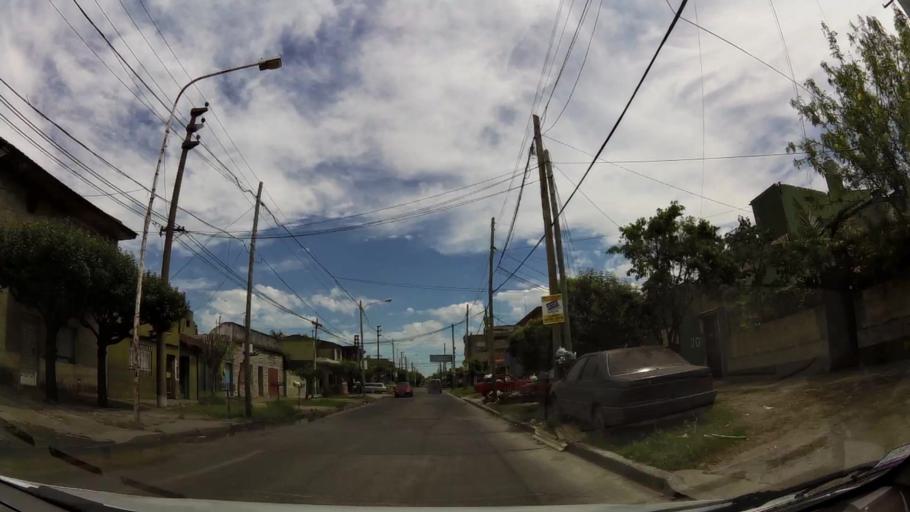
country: AR
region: Buenos Aires
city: San Justo
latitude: -34.6842
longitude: -58.5275
